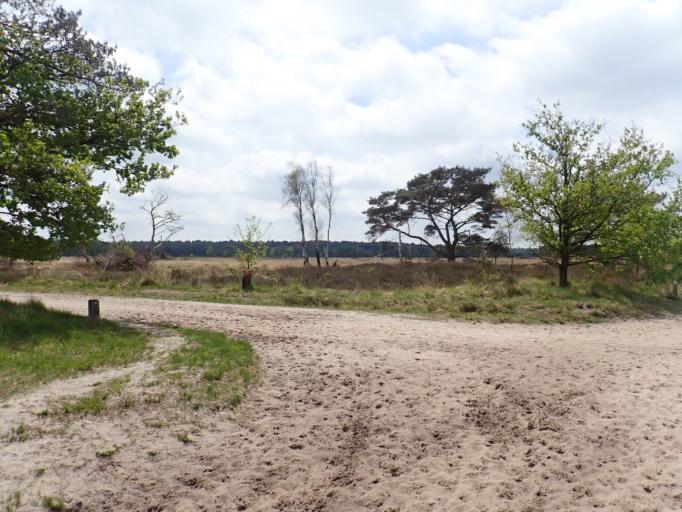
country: BE
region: Flanders
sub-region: Provincie Antwerpen
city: Kalmthout
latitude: 51.3851
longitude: 4.4379
